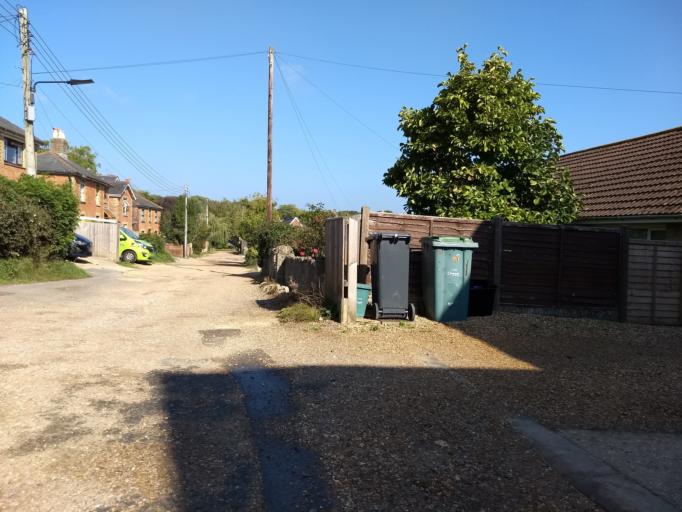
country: GB
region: England
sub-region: Isle of Wight
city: Newchurch
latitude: 50.7257
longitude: -1.2290
